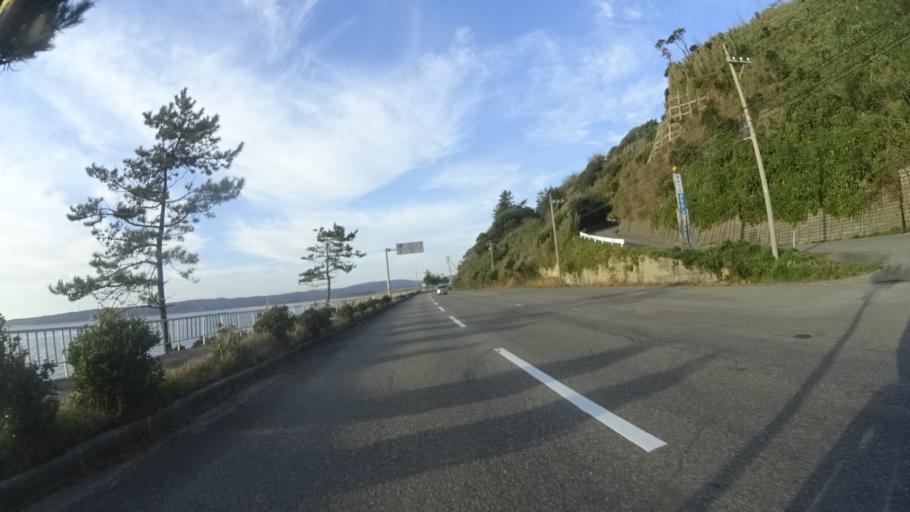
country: JP
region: Ishikawa
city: Nanao
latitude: 37.1291
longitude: 136.7274
